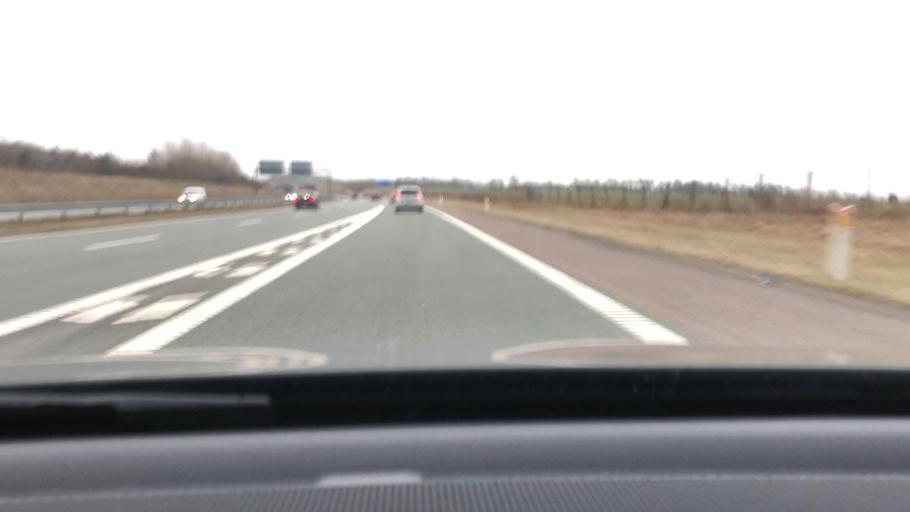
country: DK
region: South Denmark
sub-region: Vejle Kommune
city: Give
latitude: 55.8395
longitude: 9.2803
